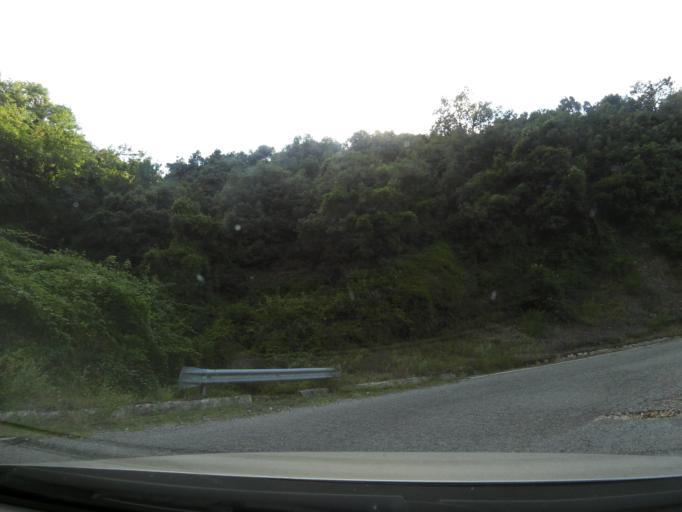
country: IT
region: Calabria
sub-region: Provincia di Reggio Calabria
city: Pazzano
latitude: 38.4678
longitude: 16.4173
